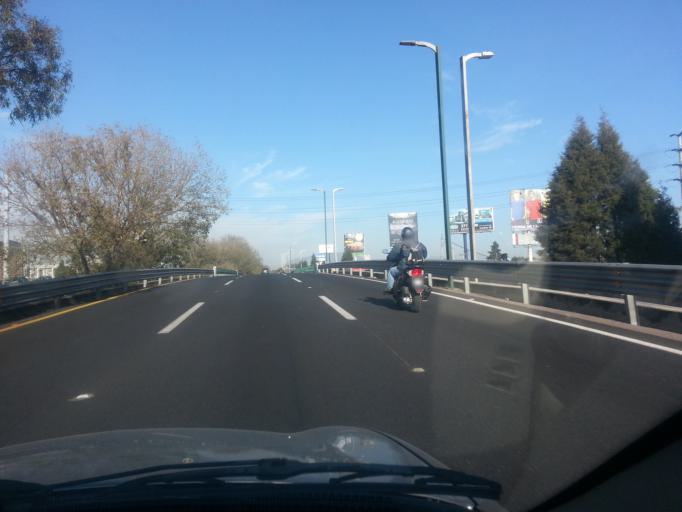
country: MX
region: Mexico
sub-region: San Mateo Atenco
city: Santa Maria la Asuncion
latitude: 19.2868
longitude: -99.5724
